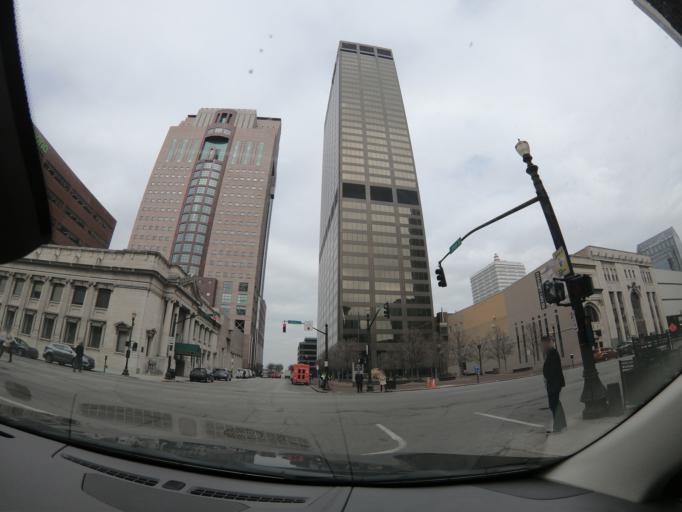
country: US
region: Kentucky
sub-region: Jefferson County
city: Louisville
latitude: 38.2554
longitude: -85.7585
